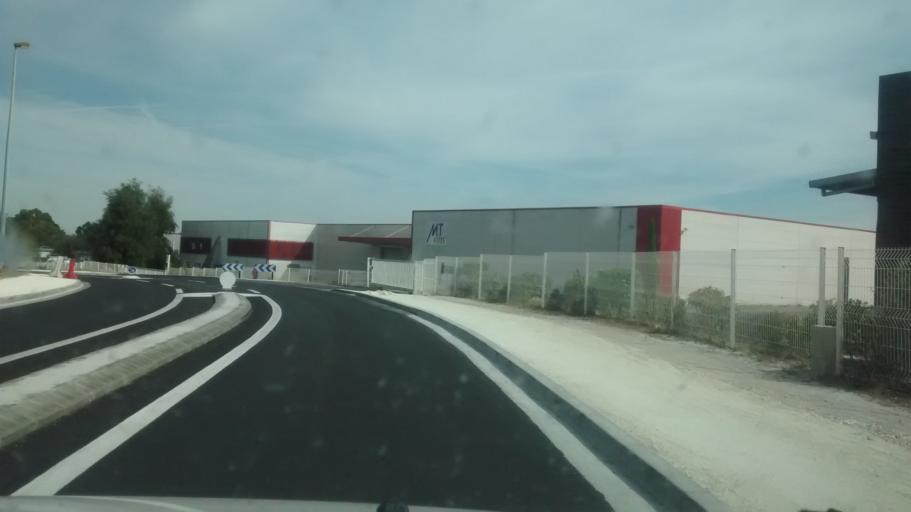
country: FR
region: Aquitaine
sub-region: Departement de la Gironde
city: Floirac
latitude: 44.8435
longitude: -0.4965
